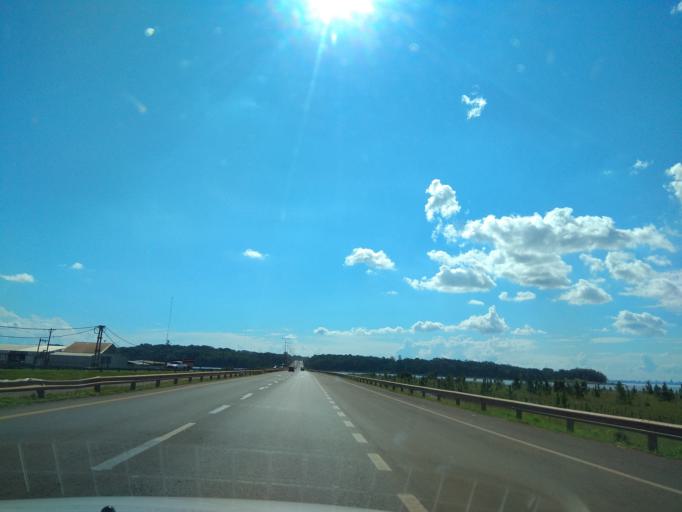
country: AR
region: Misiones
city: Garupa
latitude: -27.4654
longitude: -55.8039
